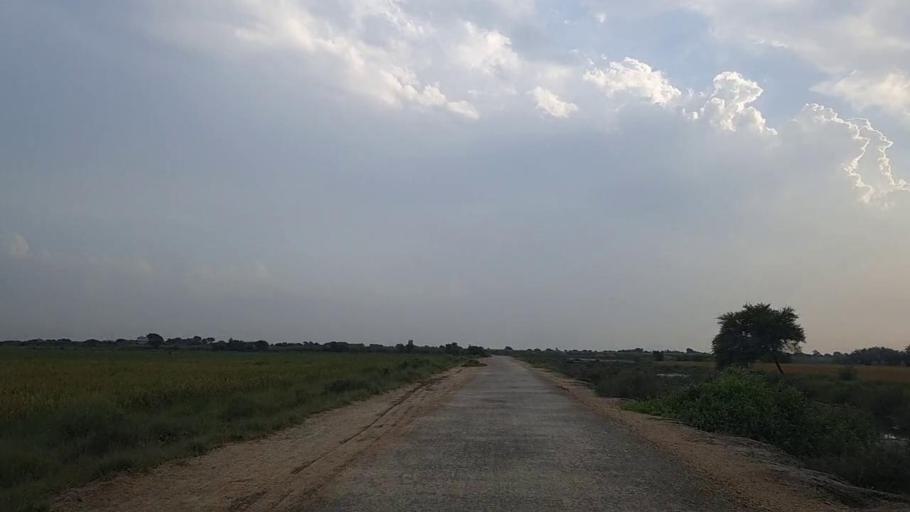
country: PK
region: Sindh
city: Daro Mehar
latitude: 24.7762
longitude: 68.1496
